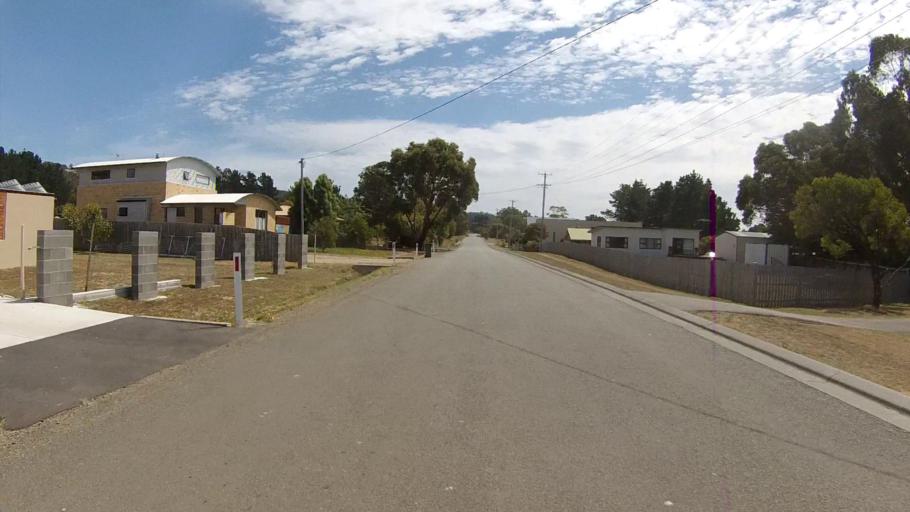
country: AU
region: Tasmania
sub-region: Clarence
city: Sandford
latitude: -42.9896
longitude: 147.5216
